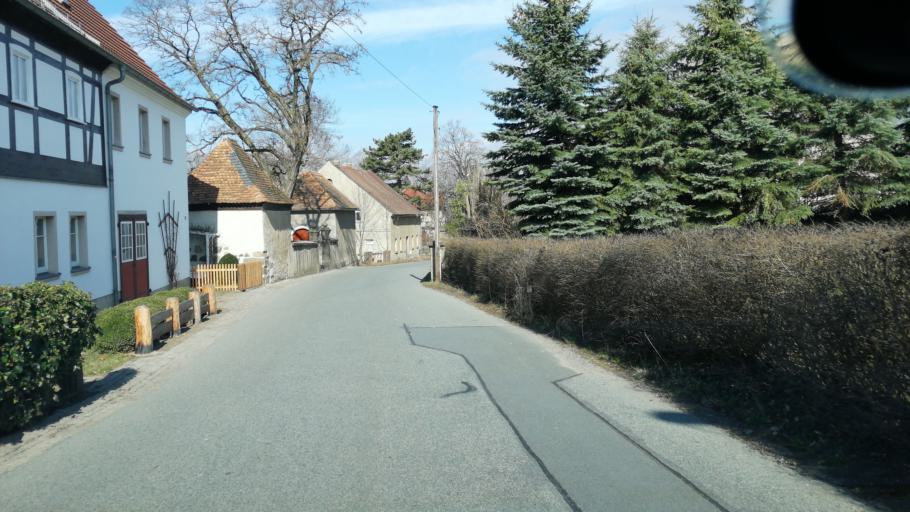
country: DE
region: Saxony
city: Niedercunnersdorf
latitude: 51.0358
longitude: 14.6708
